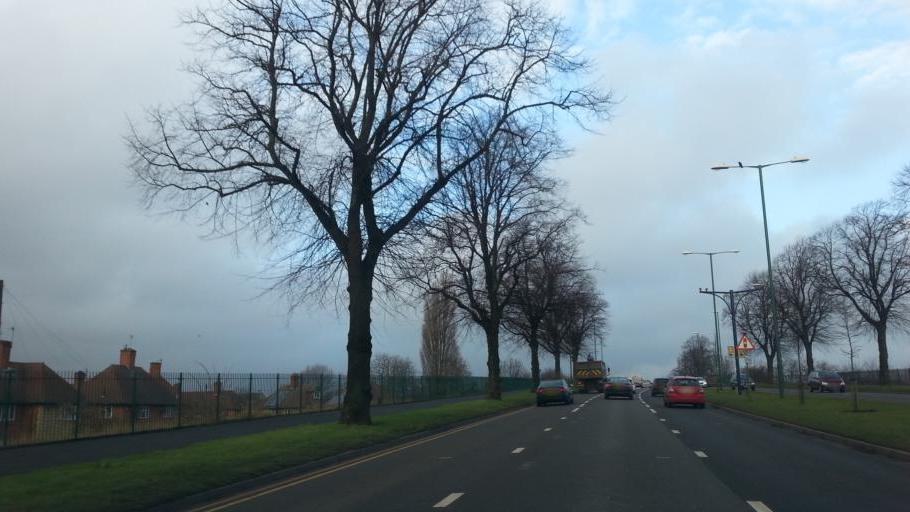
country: GB
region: England
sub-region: Nottingham
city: Nottingham
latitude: 52.9583
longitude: -1.1911
